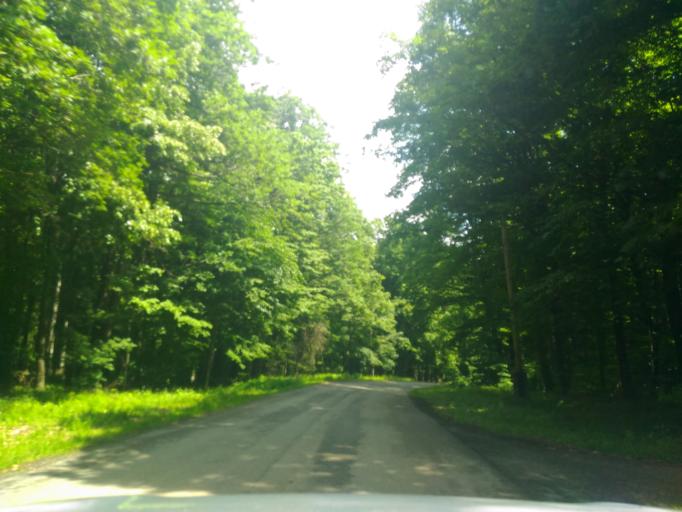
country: HU
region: Baranya
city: Pecs
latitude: 46.1261
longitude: 18.2259
